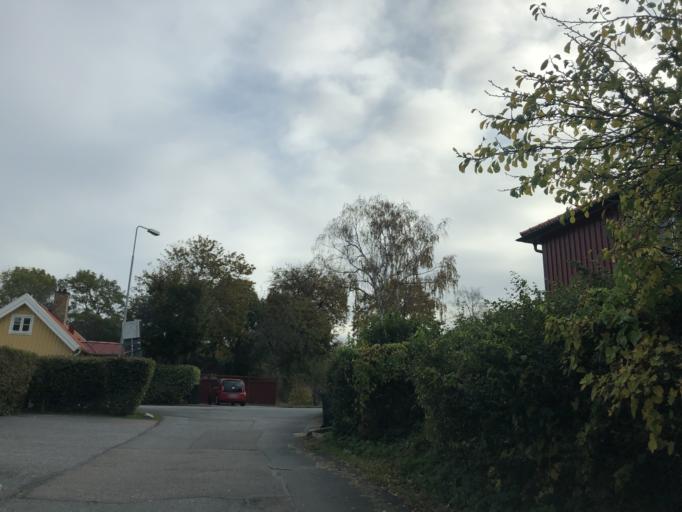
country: SE
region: Vaestra Goetaland
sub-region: Goteborg
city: Majorna
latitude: 57.6804
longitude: 11.8879
